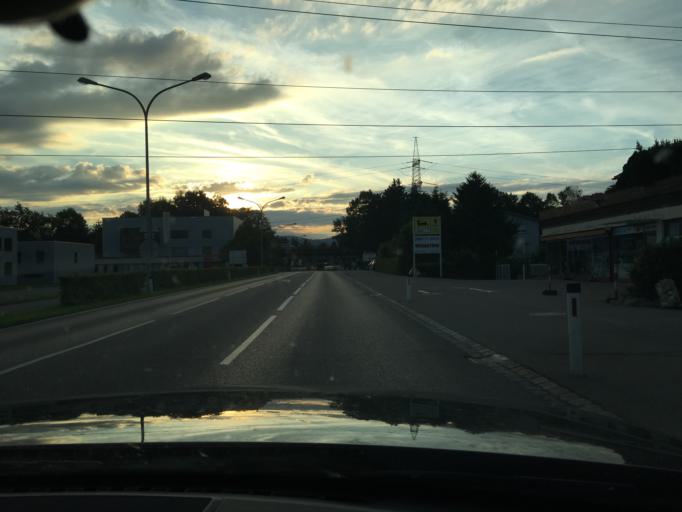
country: AT
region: Vorarlberg
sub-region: Politischer Bezirk Dornbirn
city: Hohenems
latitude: 47.3758
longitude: 9.6744
